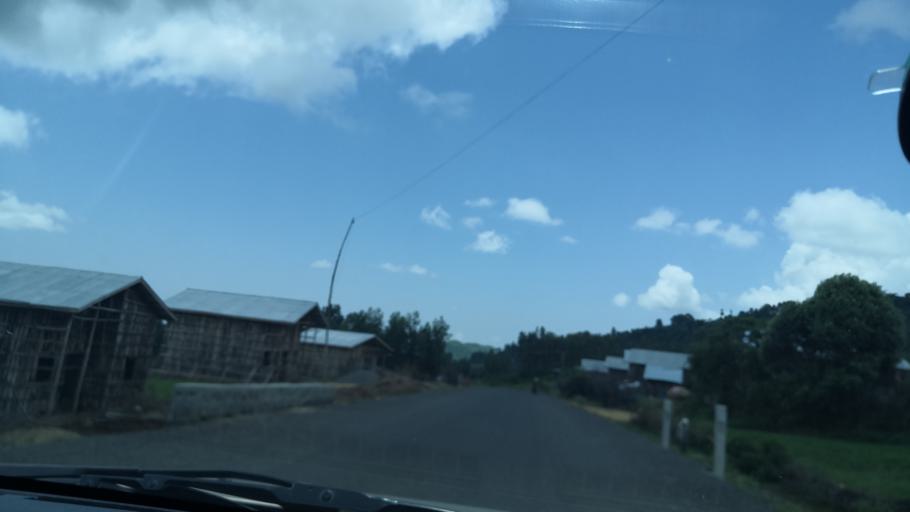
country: ET
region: Amhara
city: Abomsa
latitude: 10.3200
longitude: 39.8736
